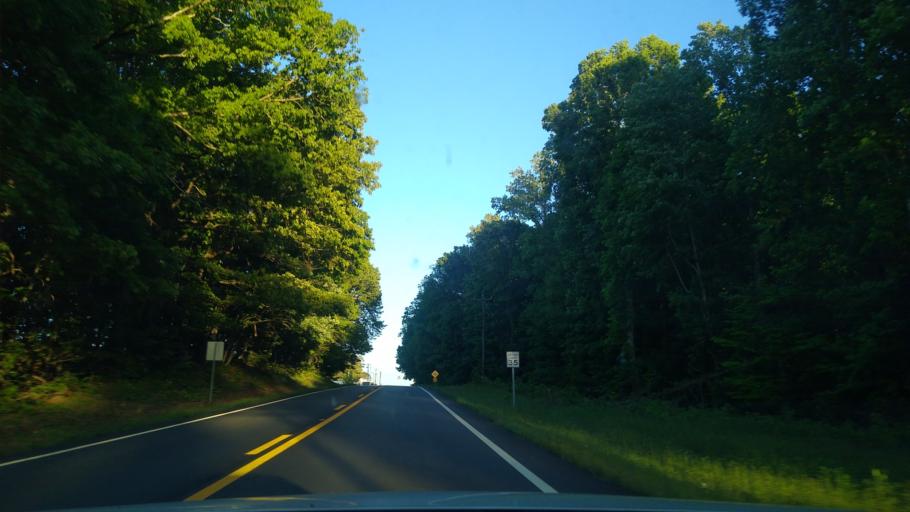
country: US
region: North Carolina
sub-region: Rockingham County
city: Reidsville
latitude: 36.3910
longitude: -79.5082
